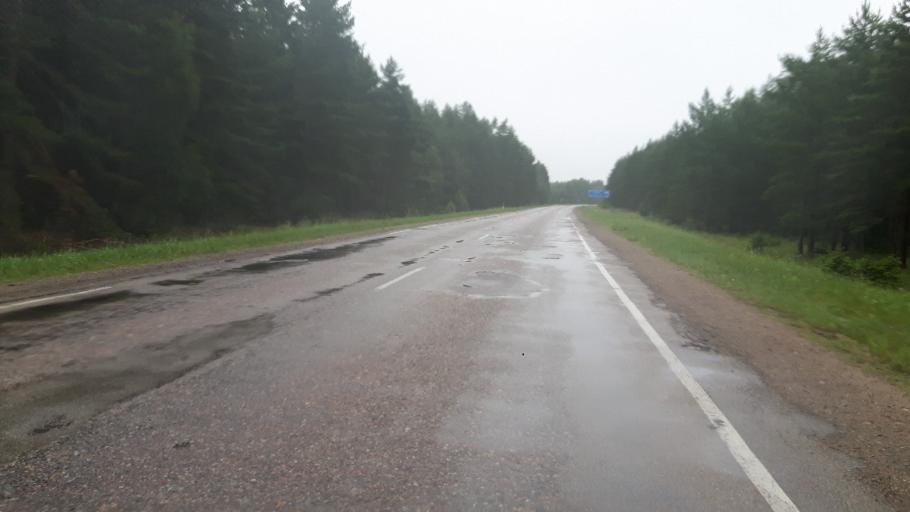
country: LT
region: Klaipedos apskritis
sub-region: Palanga
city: Sventoji
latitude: 56.0850
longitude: 21.1238
